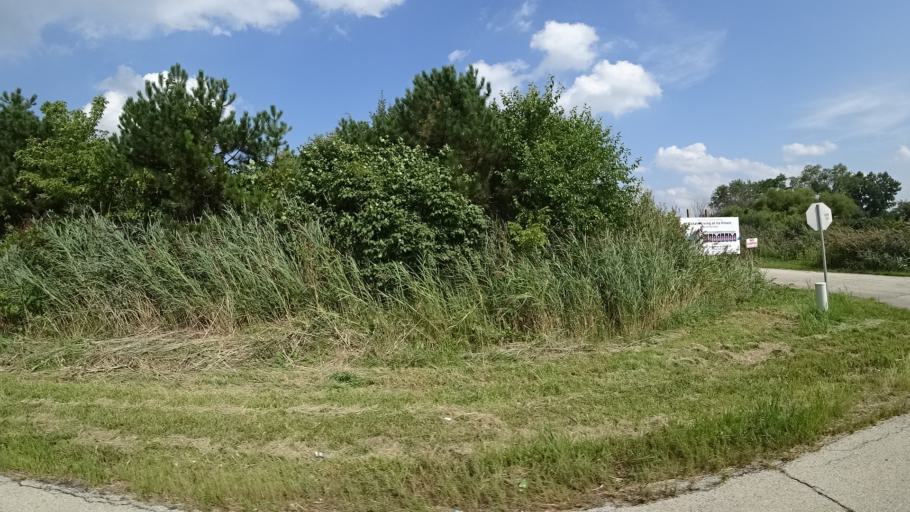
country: US
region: Illinois
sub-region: Will County
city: Goodings Grove
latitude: 41.6498
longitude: -87.8927
